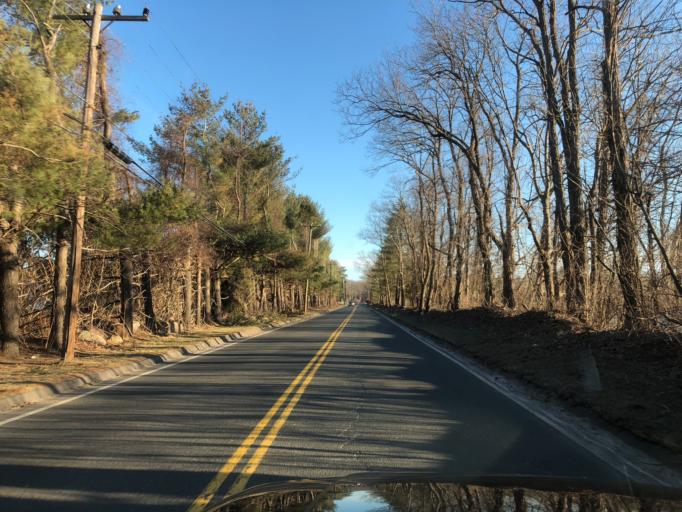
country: US
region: Connecticut
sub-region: Hartford County
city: Farmington
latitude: 41.7452
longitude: -72.8538
